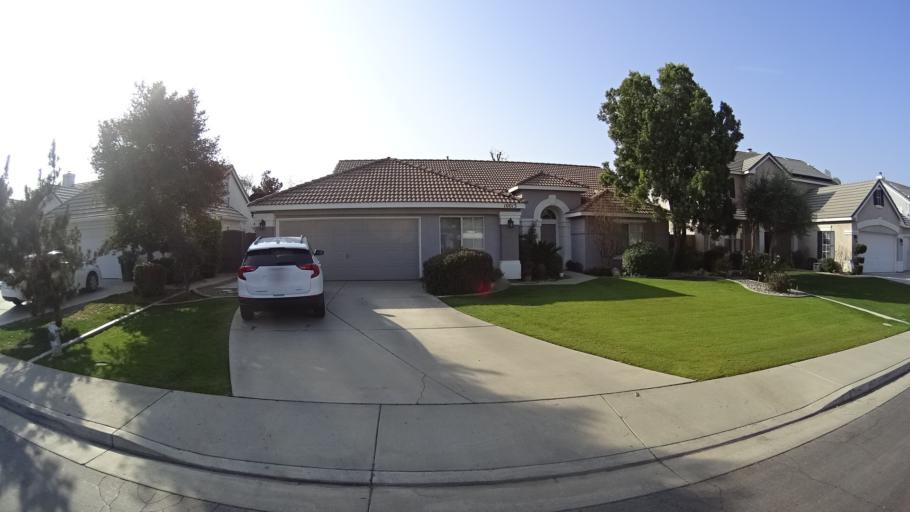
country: US
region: California
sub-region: Kern County
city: Greenacres
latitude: 35.4104
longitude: -119.1140
